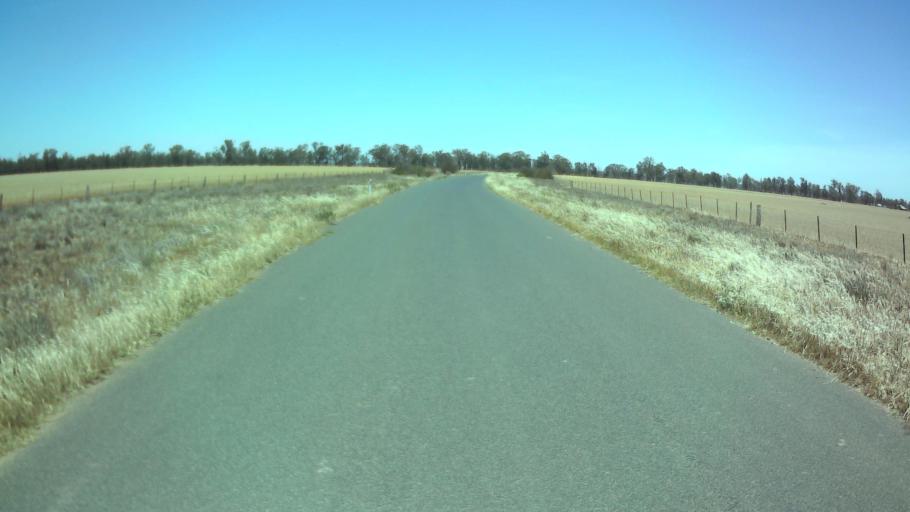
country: AU
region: New South Wales
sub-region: Weddin
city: Grenfell
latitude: -34.0691
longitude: 147.7774
